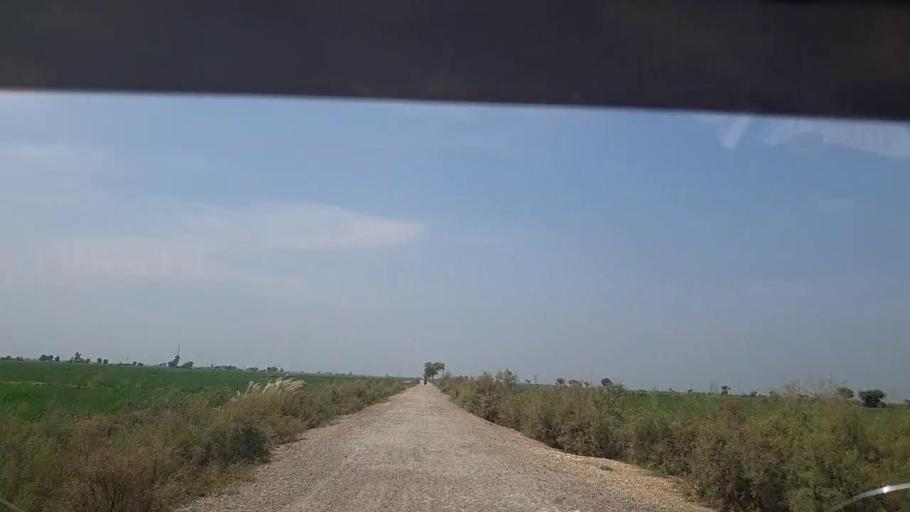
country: PK
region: Sindh
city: Thul
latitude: 28.2131
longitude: 68.6842
